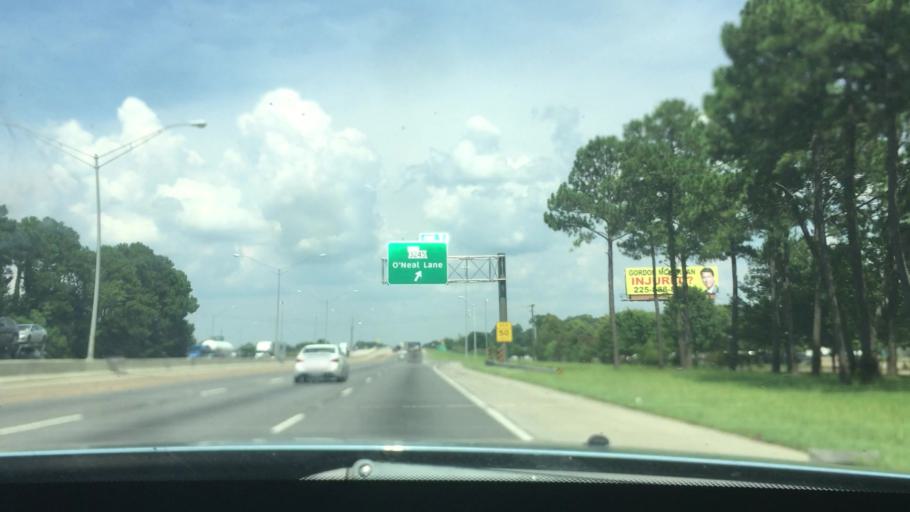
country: US
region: Louisiana
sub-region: East Baton Rouge Parish
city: Shenandoah
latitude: 30.4409
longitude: -91.0130
